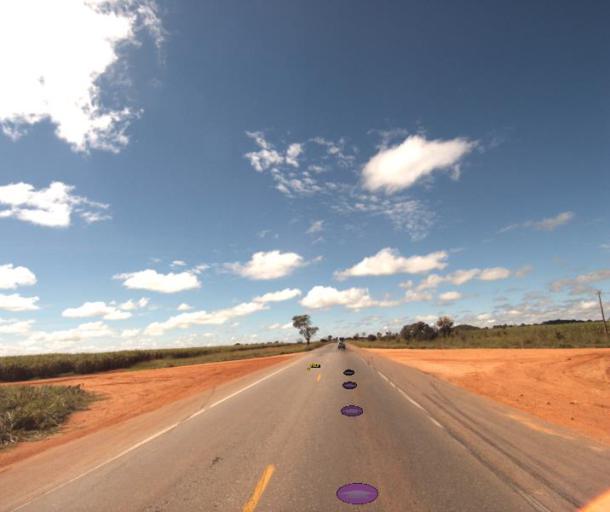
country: BR
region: Goias
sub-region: Rialma
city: Rialma
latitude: -15.4111
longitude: -49.5272
